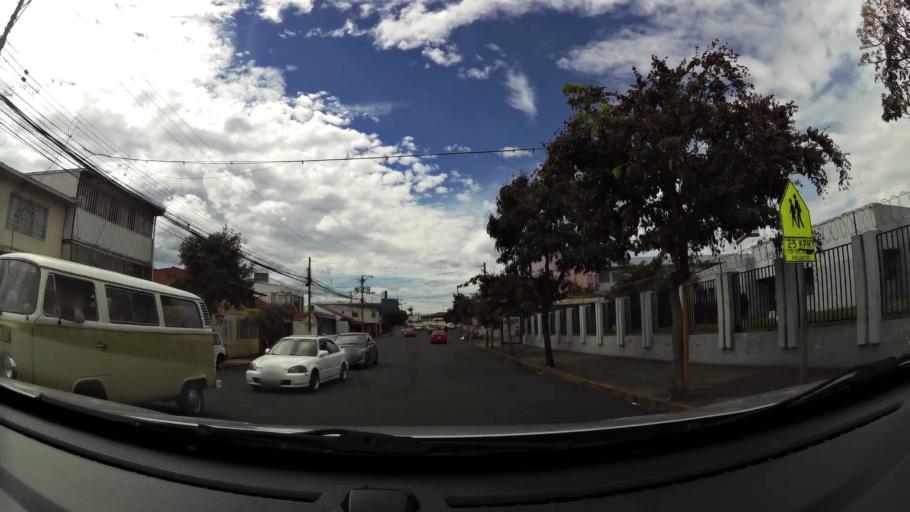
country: CR
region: San Jose
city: San Jose
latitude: 9.9238
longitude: -84.0780
